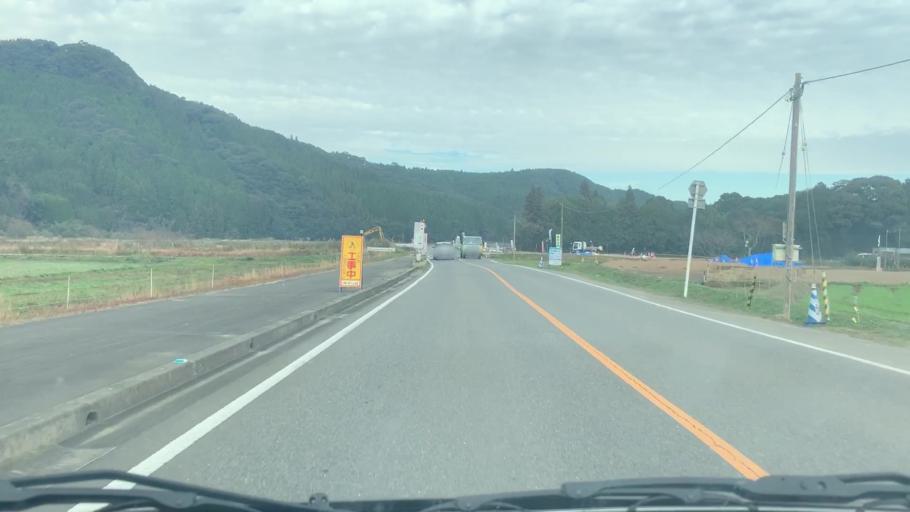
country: JP
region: Saga Prefecture
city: Takeocho-takeo
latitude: 33.2460
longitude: 129.9693
